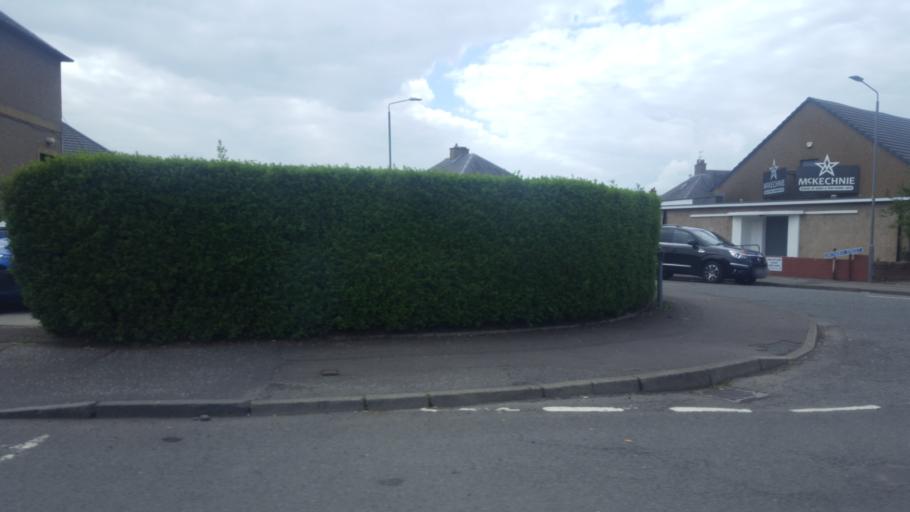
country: GB
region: Scotland
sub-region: Falkirk
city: Grangemouth
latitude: 56.0101
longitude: -3.7238
